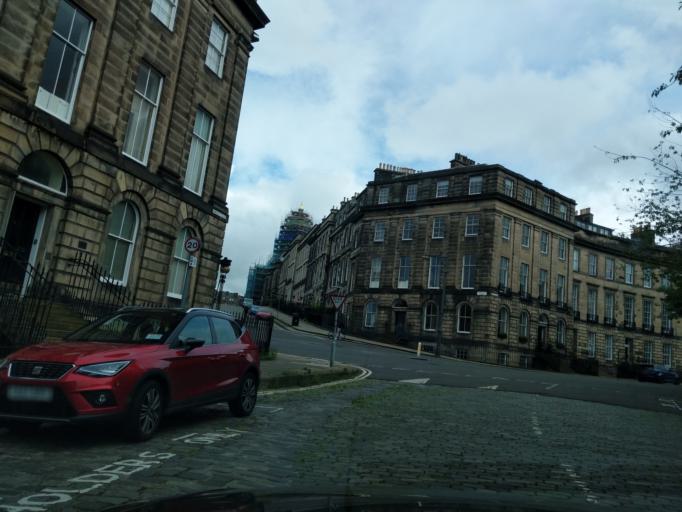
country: GB
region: Scotland
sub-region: Edinburgh
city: Edinburgh
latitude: 55.9534
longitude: -3.2096
